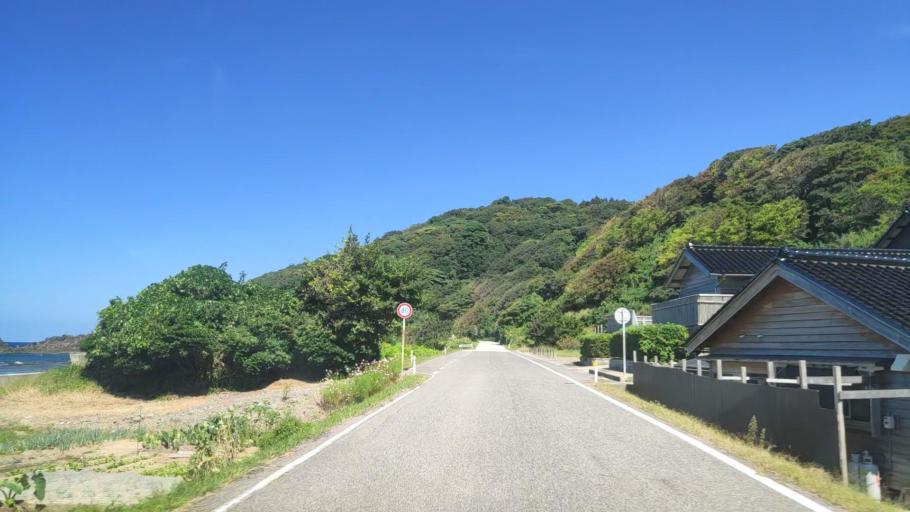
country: JP
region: Ishikawa
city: Nanao
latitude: 37.5204
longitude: 137.2461
